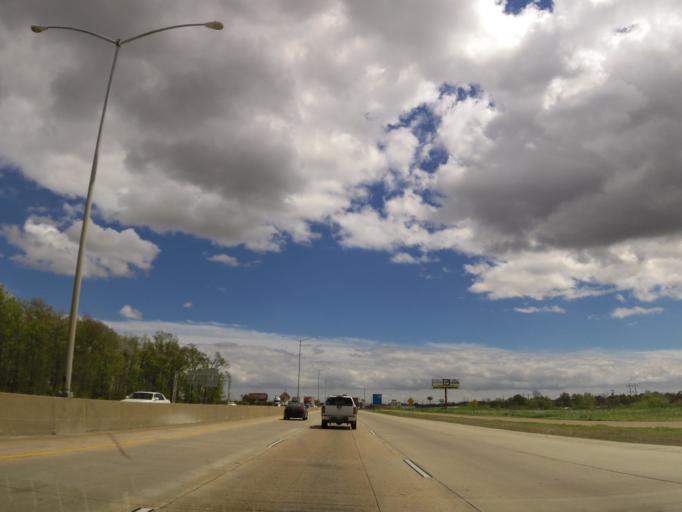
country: US
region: Arkansas
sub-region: Crittenden County
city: West Memphis
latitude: 35.1627
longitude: -90.1698
